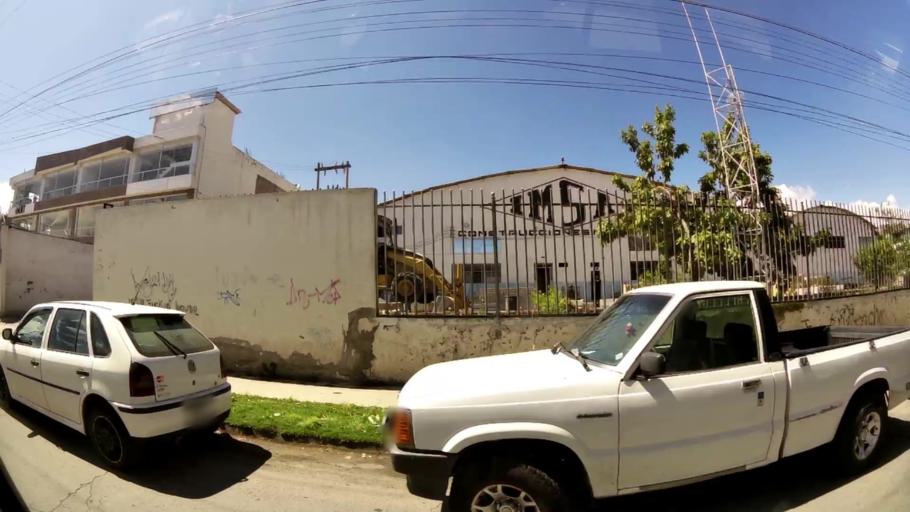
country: EC
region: Chimborazo
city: Riobamba
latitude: -1.6809
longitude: -78.6306
